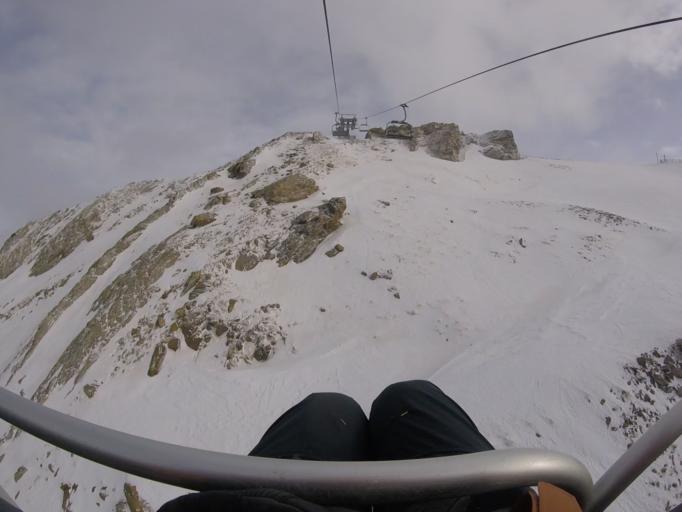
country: AD
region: Canillo
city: Canillo
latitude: 42.5528
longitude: 1.6266
